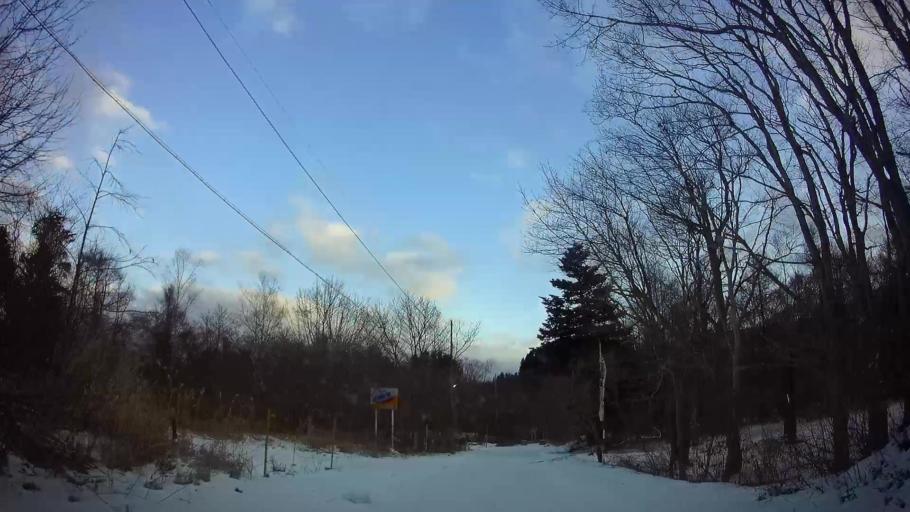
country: JP
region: Hokkaido
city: Nanae
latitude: 42.0192
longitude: 140.8428
